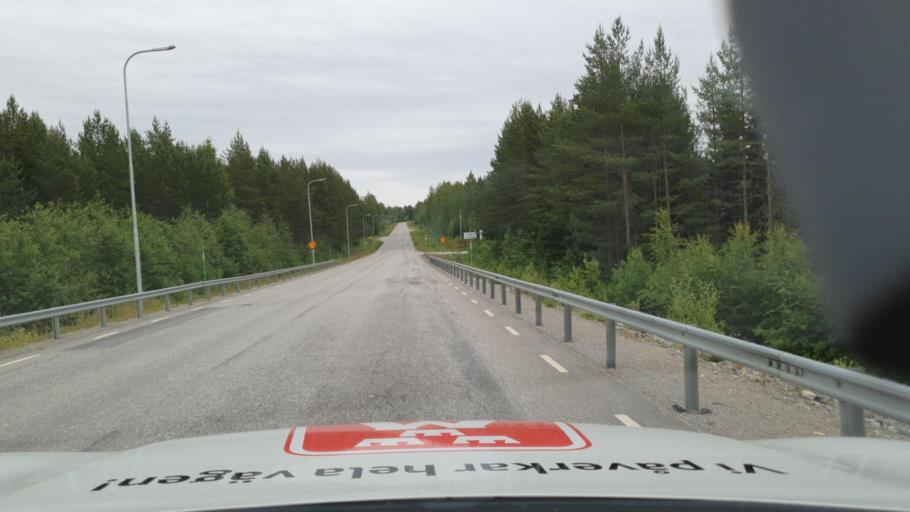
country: SE
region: Vaesterbotten
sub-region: Nordmalings Kommun
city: Nordmaling
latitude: 63.5486
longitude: 19.4197
